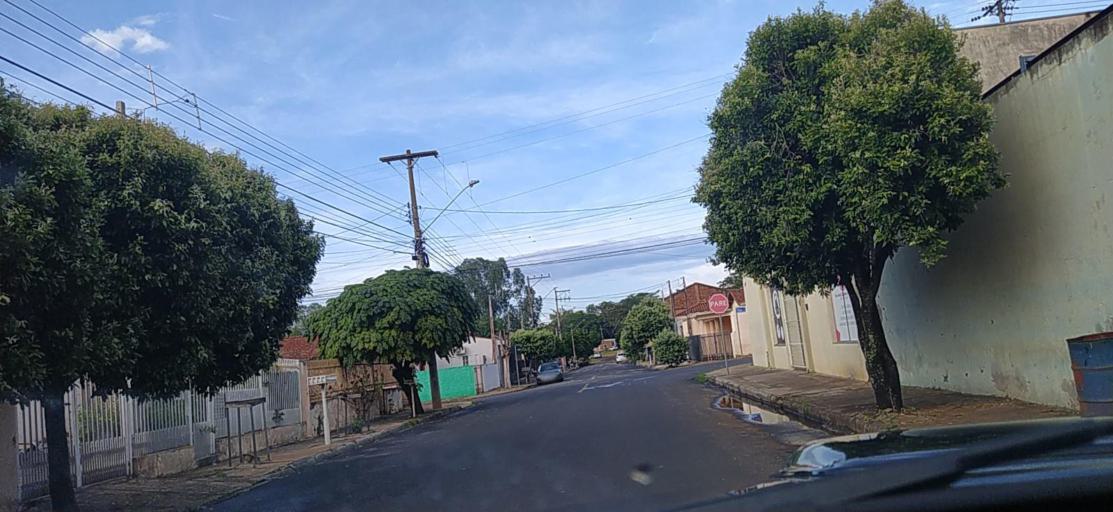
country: BR
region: Sao Paulo
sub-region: Pindorama
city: Pindorama
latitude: -21.1858
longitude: -48.9025
